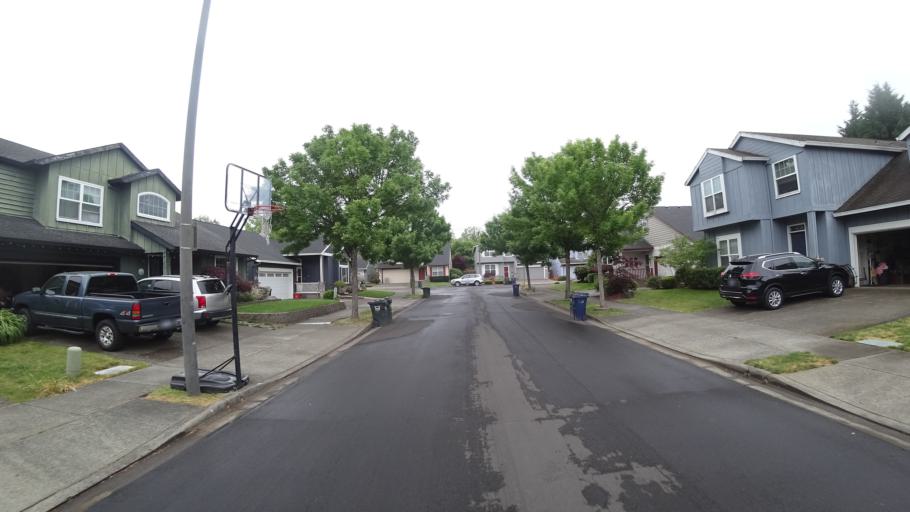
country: US
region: Oregon
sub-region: Washington County
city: Rockcreek
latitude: 45.5310
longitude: -122.8903
